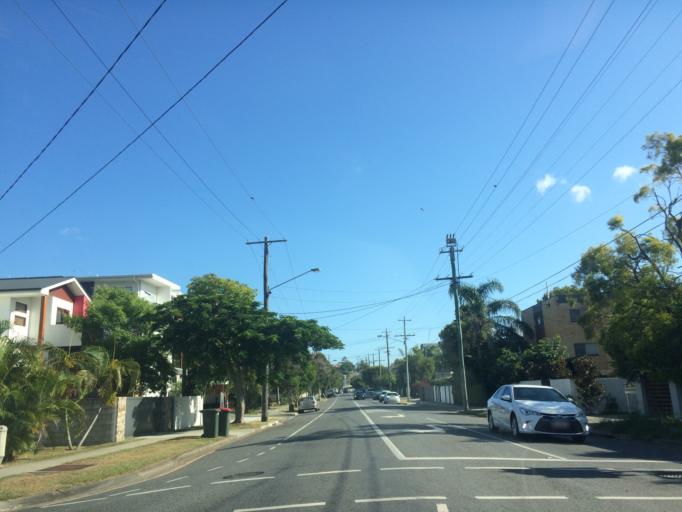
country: AU
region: Queensland
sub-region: Brisbane
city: Balmoral
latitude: -27.4566
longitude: 153.0614
